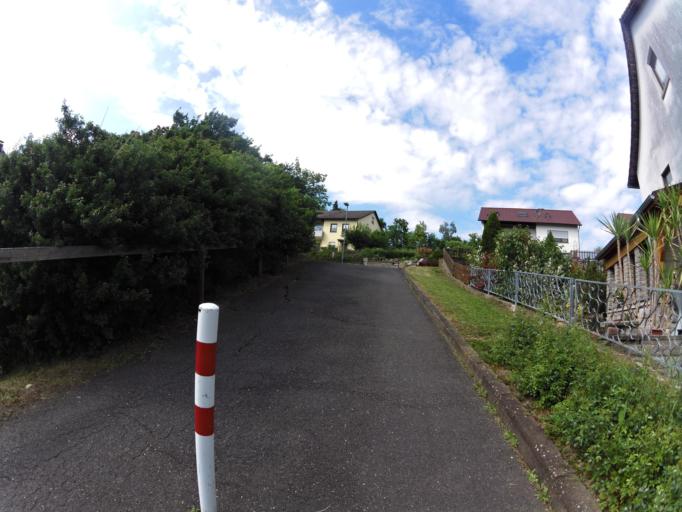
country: DE
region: Bavaria
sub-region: Regierungsbezirk Unterfranken
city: Gaukonigshofen
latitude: 49.6541
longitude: 10.0204
